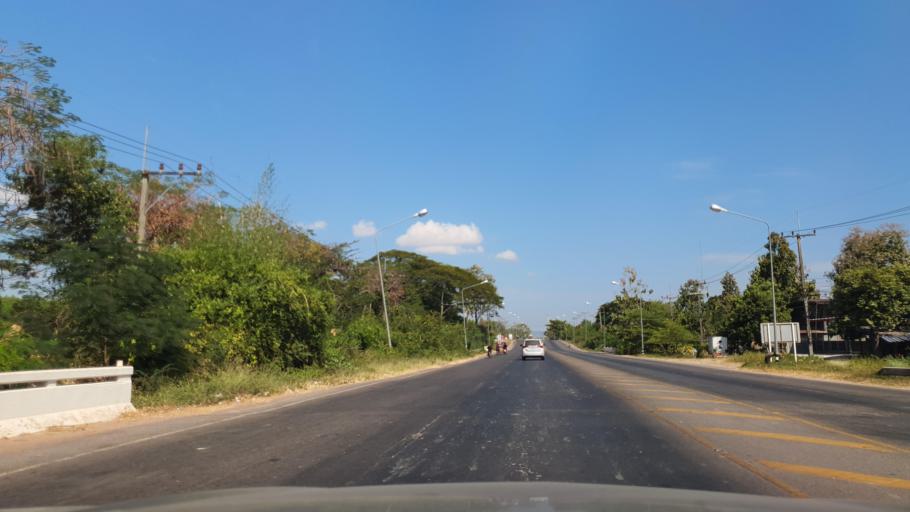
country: TH
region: Kalasin
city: Somdet
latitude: 16.7118
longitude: 103.7528
